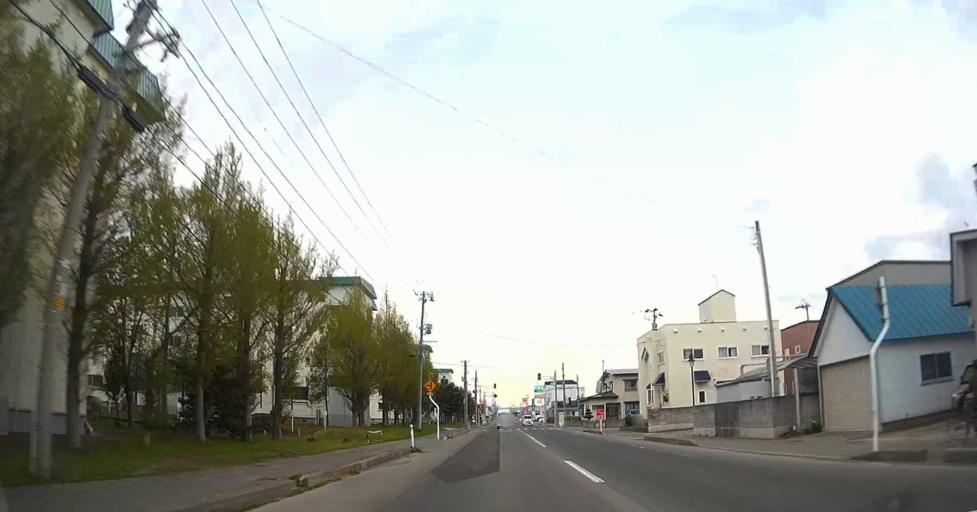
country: JP
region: Aomori
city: Aomori Shi
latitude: 40.8584
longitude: 140.6813
